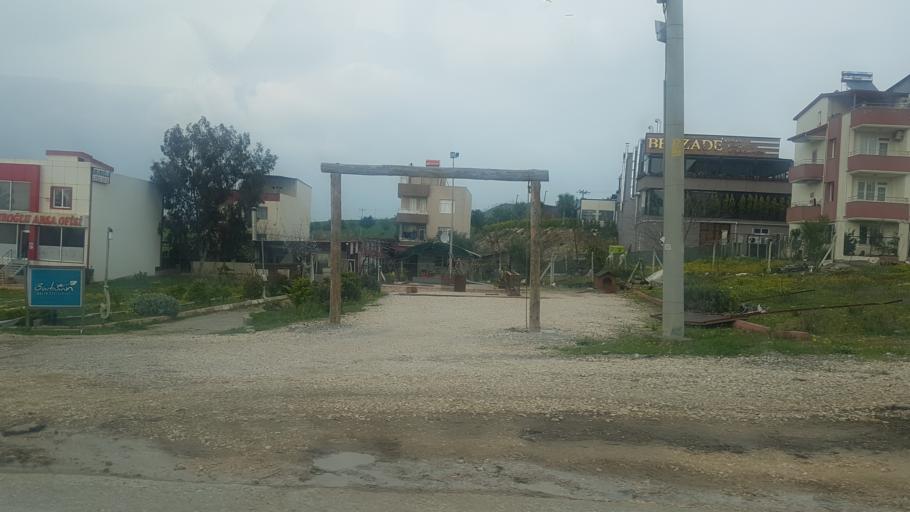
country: TR
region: Adana
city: Seyhan
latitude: 37.0575
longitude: 35.2440
